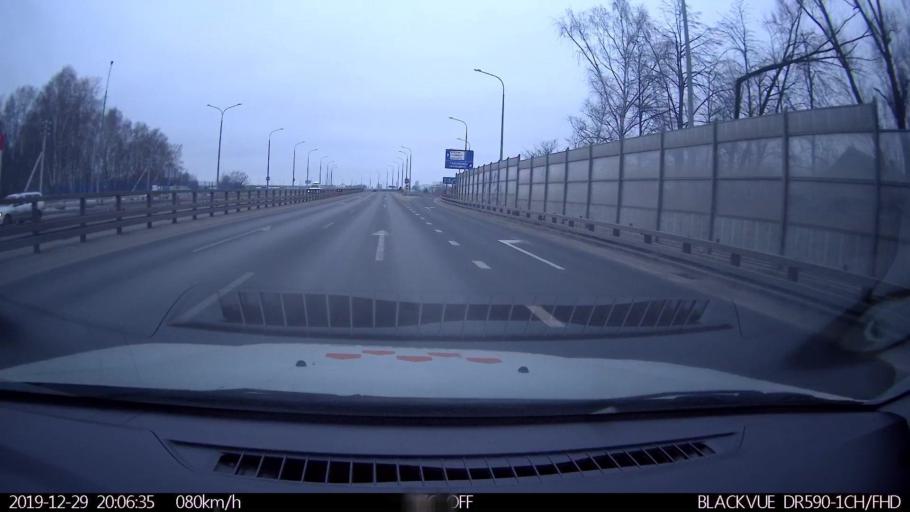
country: RU
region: Nizjnij Novgorod
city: Neklyudovo
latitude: 56.3964
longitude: 44.0000
